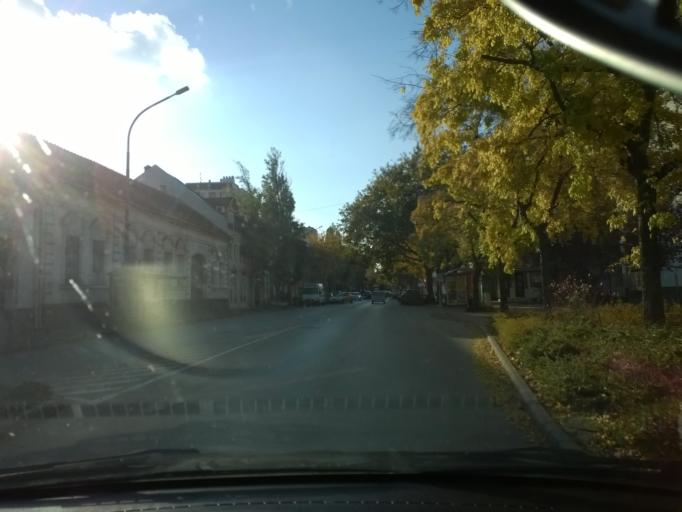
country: HU
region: Csongrad
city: Szentes
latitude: 46.6517
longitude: 20.2654
